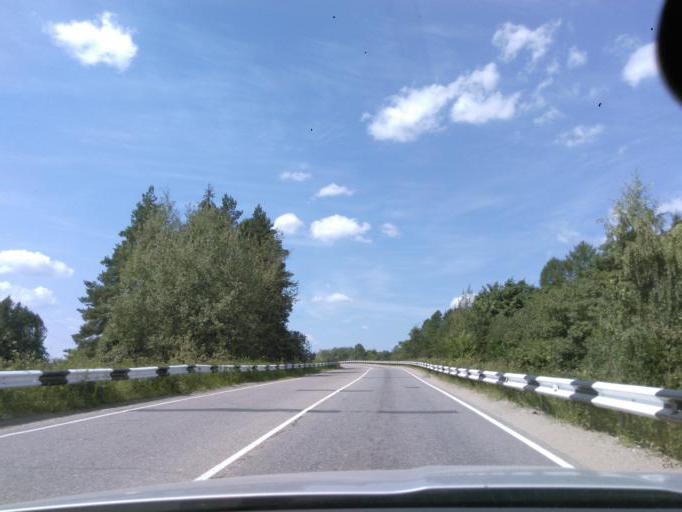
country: RU
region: Moskovskaya
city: Solnechnogorsk
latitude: 56.1658
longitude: 36.9998
